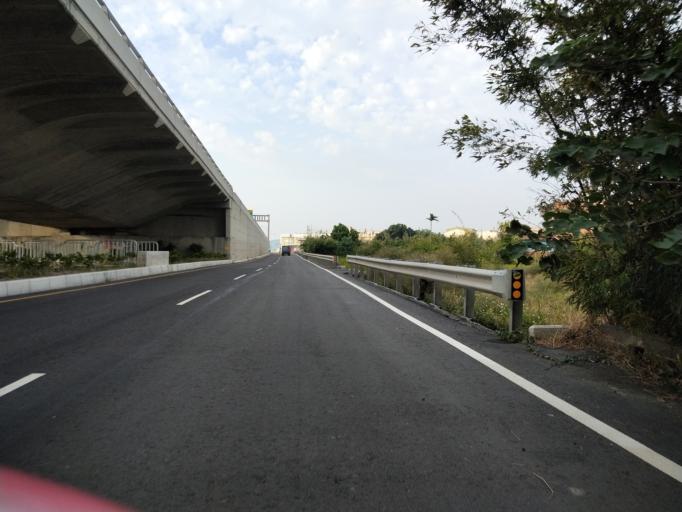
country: TW
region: Taiwan
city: Fengyuan
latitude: 24.3617
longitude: 120.5856
